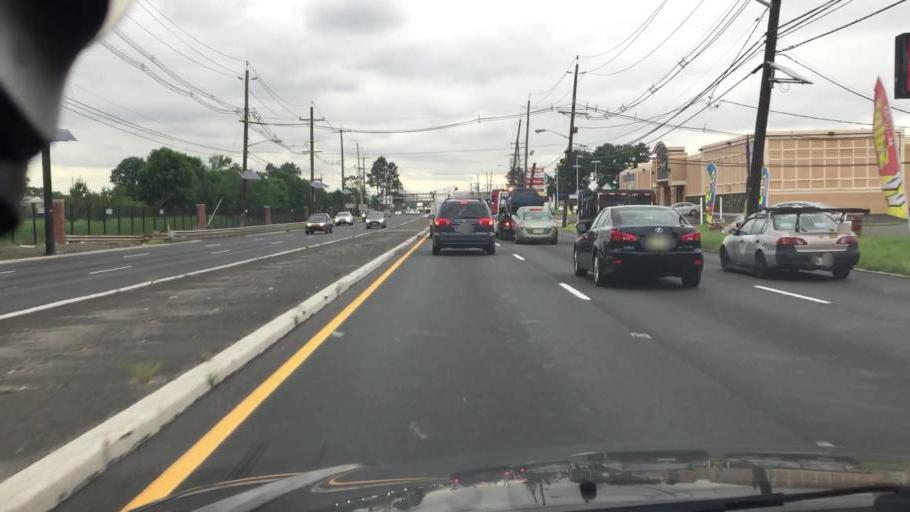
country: US
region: New Jersey
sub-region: Union County
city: Linden
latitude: 40.6116
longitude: -74.2571
